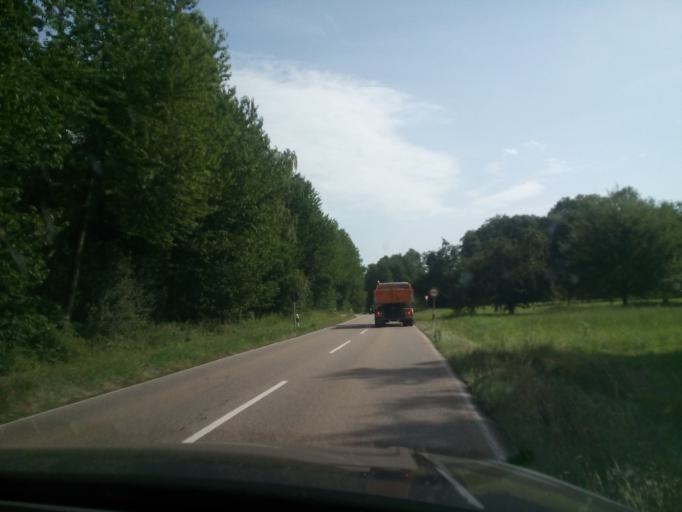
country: DE
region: Baden-Wuerttemberg
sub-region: Karlsruhe Region
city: Kuppenheim
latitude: 48.8195
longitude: 8.2448
